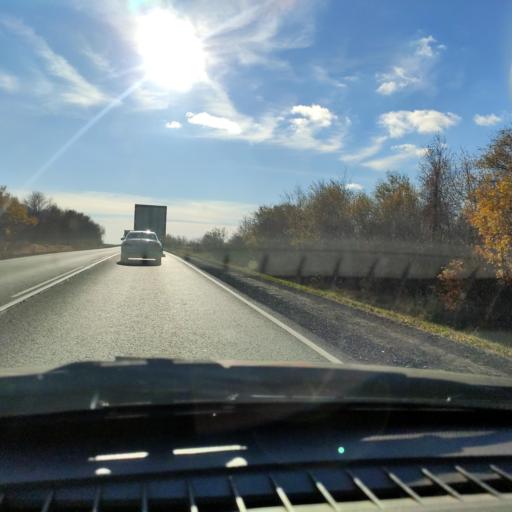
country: RU
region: Samara
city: Zhigulevsk
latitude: 53.3113
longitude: 49.3569
